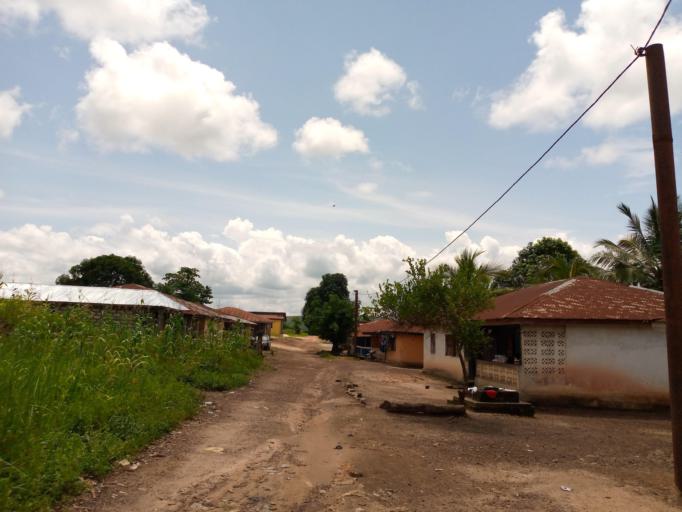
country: SL
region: Northern Province
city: Magburaka
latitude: 8.7184
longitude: -11.9609
